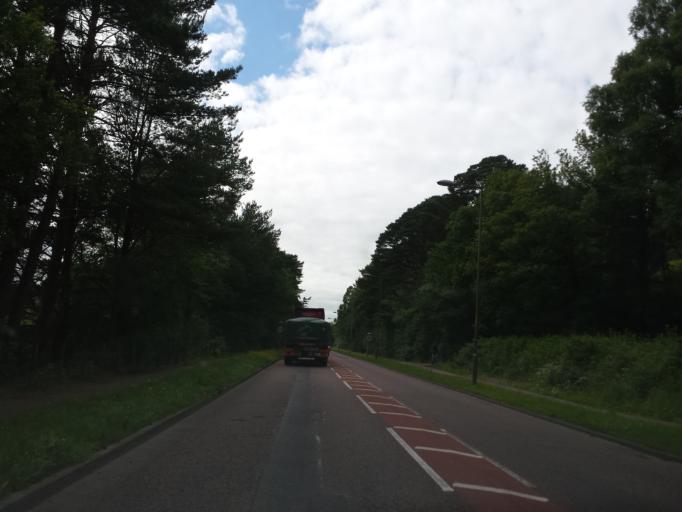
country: GB
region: Scotland
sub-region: Highland
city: Fort William
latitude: 56.8452
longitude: -5.1037
